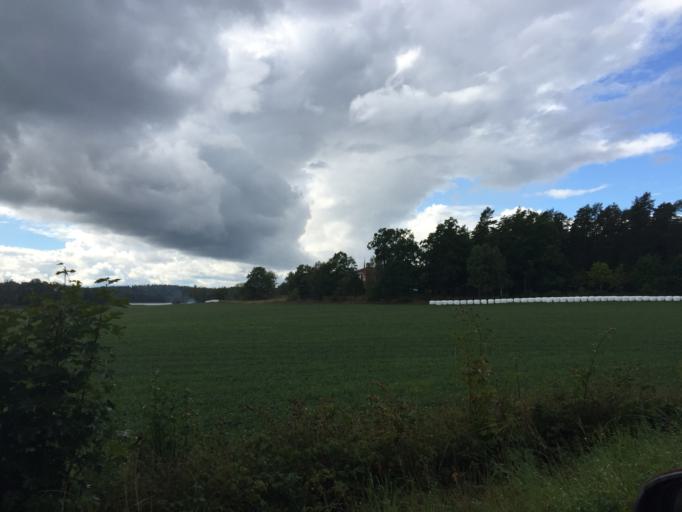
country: SE
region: Kalmar
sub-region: Vasterviks Kommun
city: Gamleby
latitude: 57.8050
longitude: 16.4630
